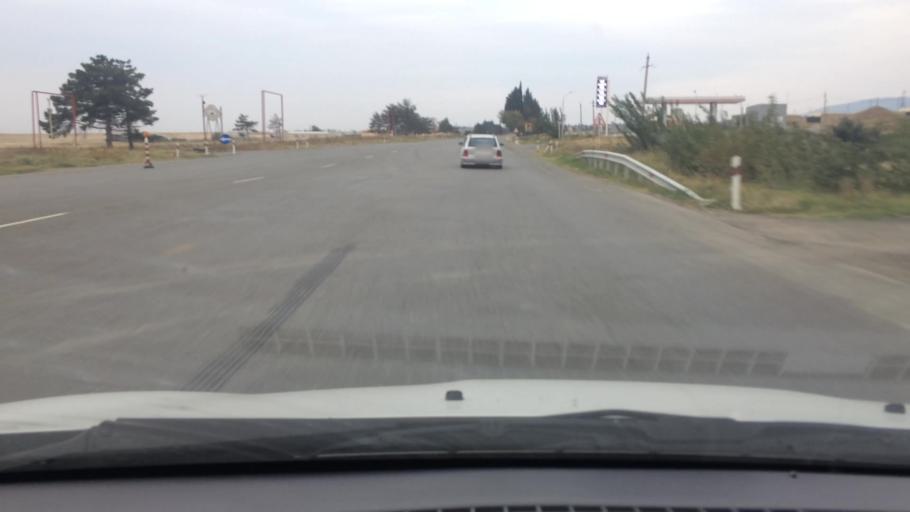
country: GE
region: T'bilisi
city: Tbilisi
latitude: 41.6434
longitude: 44.8920
